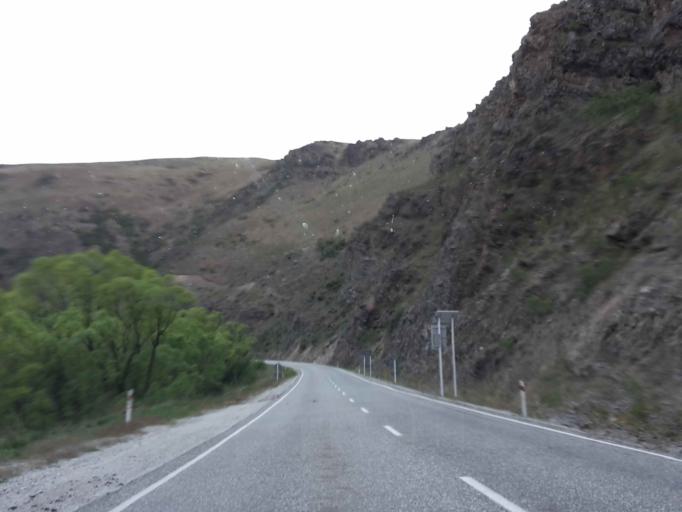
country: NZ
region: Otago
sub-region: Queenstown-Lakes District
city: Wanaka
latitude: -44.6939
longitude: 169.4849
